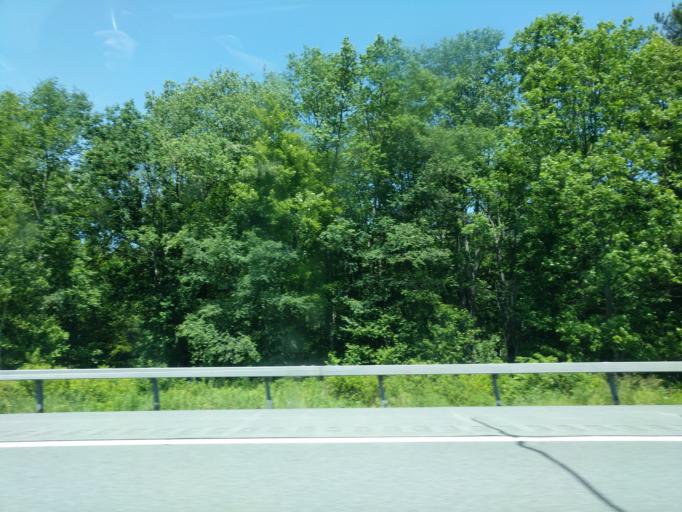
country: US
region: New York
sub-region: Sullivan County
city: Livingston Manor
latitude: 41.9252
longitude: -74.8422
